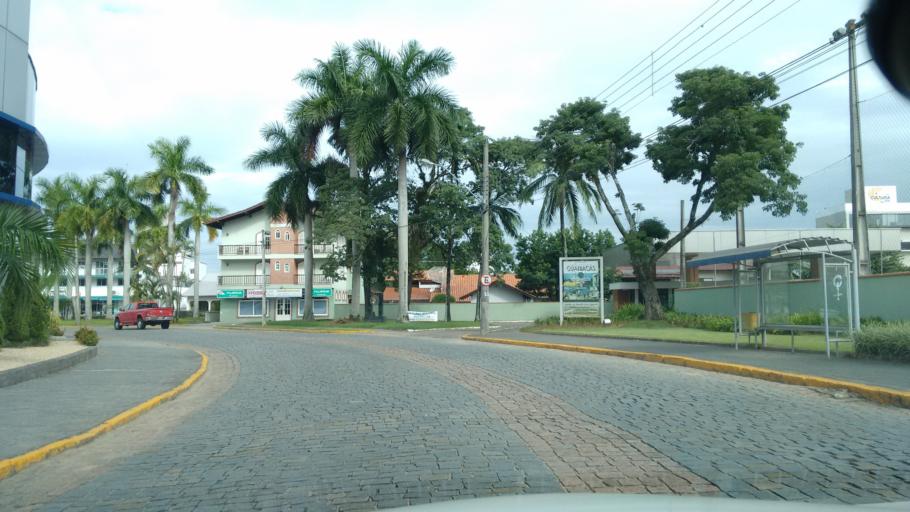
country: BR
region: Santa Catarina
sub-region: Timbo
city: Timbo
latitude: -26.8282
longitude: -49.2714
